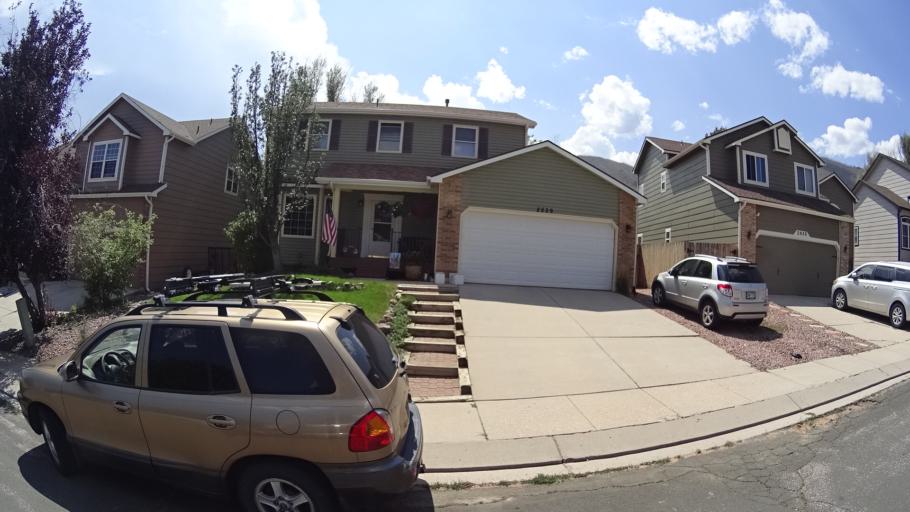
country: US
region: Colorado
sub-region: El Paso County
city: Air Force Academy
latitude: 38.9368
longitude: -104.8798
